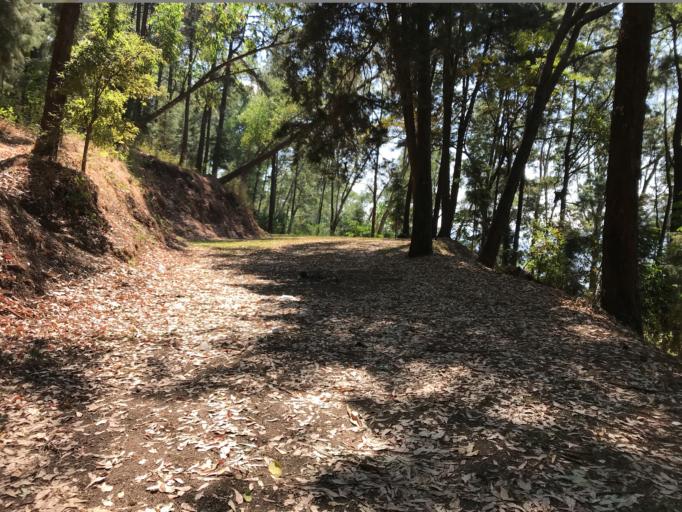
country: GT
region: Guatemala
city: Villa Canales
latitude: 14.4798
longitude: -90.5496
